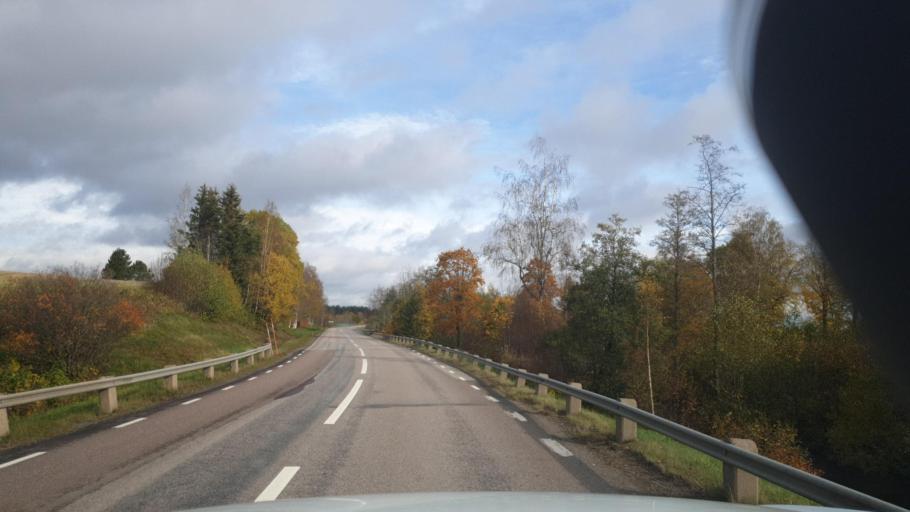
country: SE
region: Vaermland
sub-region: Sunne Kommun
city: Sunne
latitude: 59.7229
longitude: 13.1177
